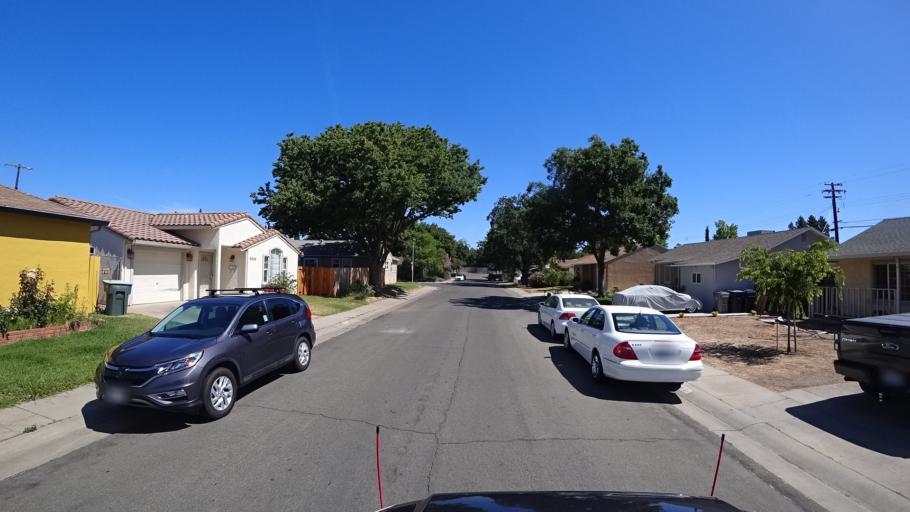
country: US
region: California
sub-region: Sacramento County
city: Parkway
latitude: 38.5198
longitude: -121.5004
